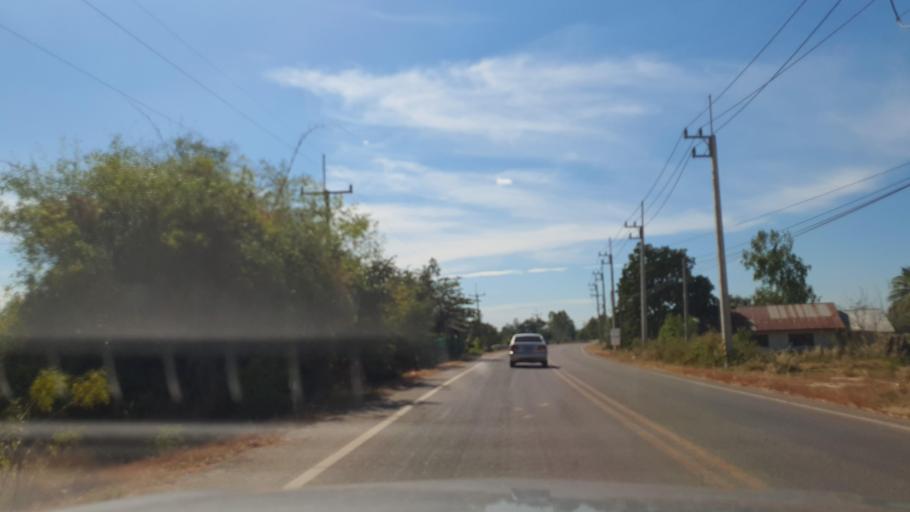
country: TH
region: Kalasin
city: Khao Wong
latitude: 16.7462
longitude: 104.1125
